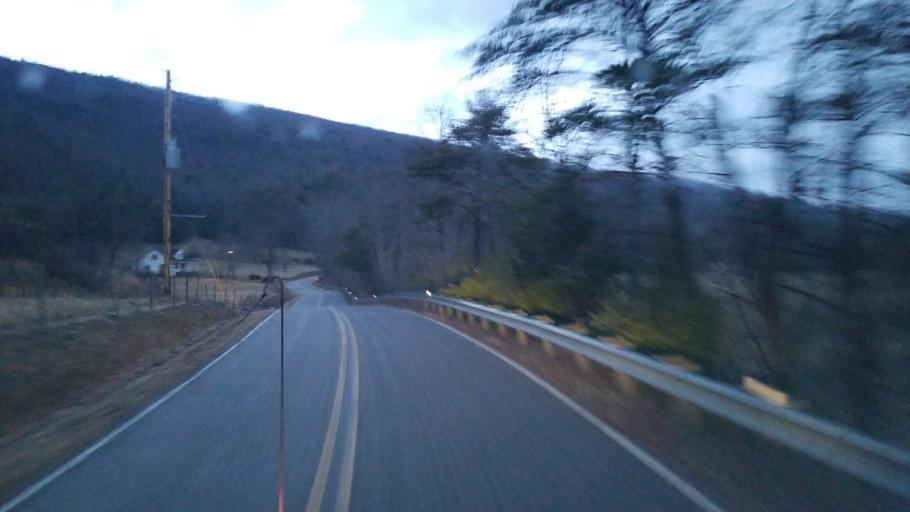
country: US
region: Virginia
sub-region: Pulaski County
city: Pulaski
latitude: 37.1348
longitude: -80.8521
